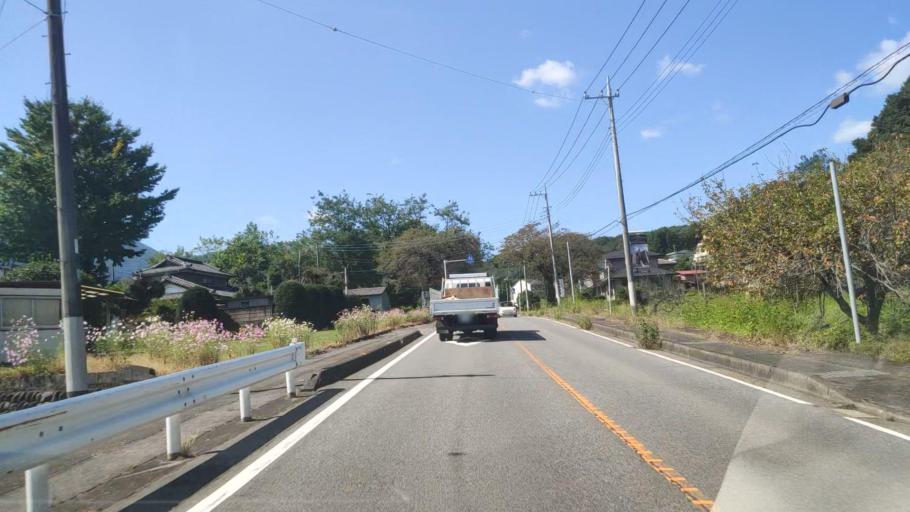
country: JP
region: Gunma
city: Shibukawa
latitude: 36.5012
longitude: 138.9635
